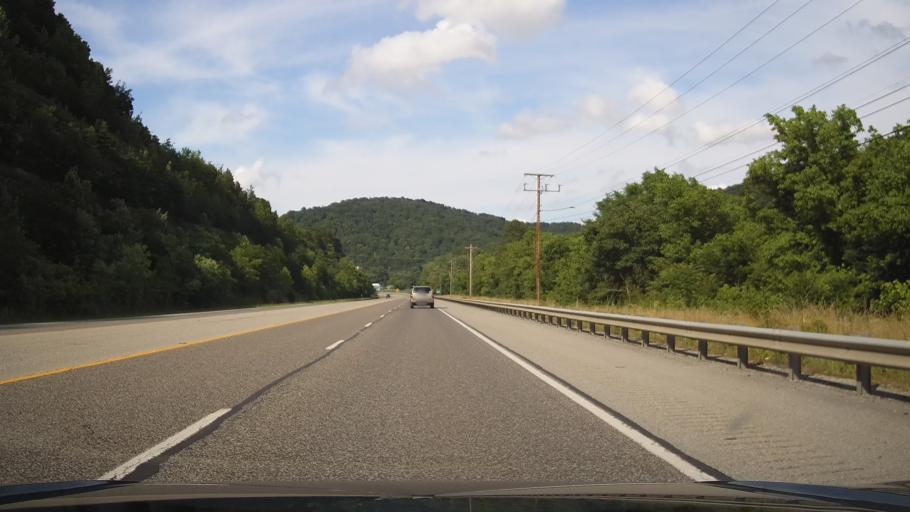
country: US
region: Kentucky
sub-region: Lawrence County
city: Louisa
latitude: 37.9887
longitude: -82.6650
